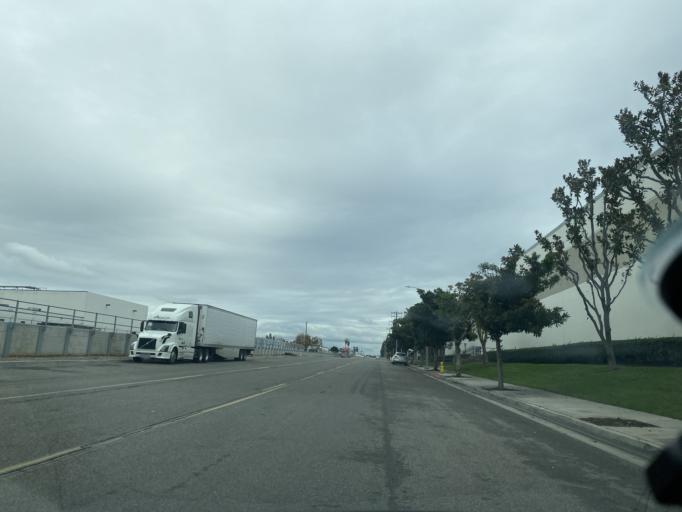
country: US
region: California
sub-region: Orange County
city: Fullerton
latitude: 33.8667
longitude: -117.9019
